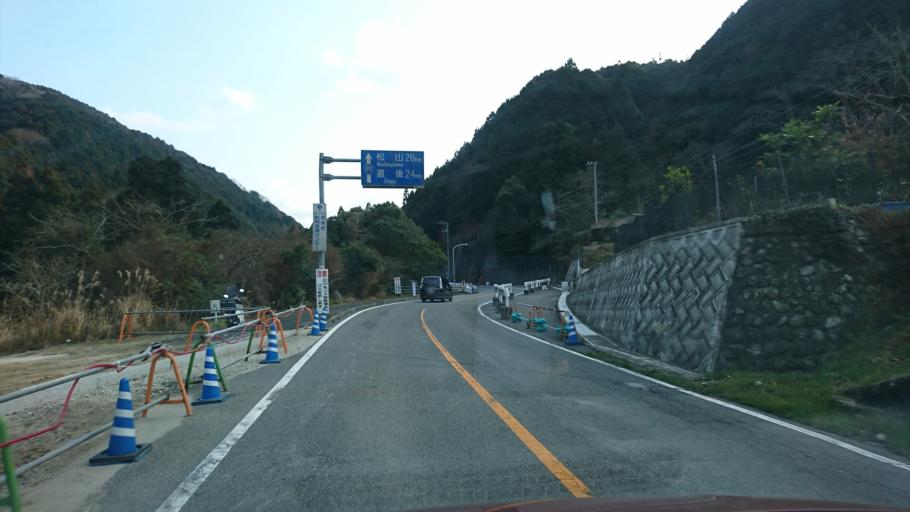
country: JP
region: Ehime
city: Hojo
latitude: 33.9677
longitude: 132.9047
